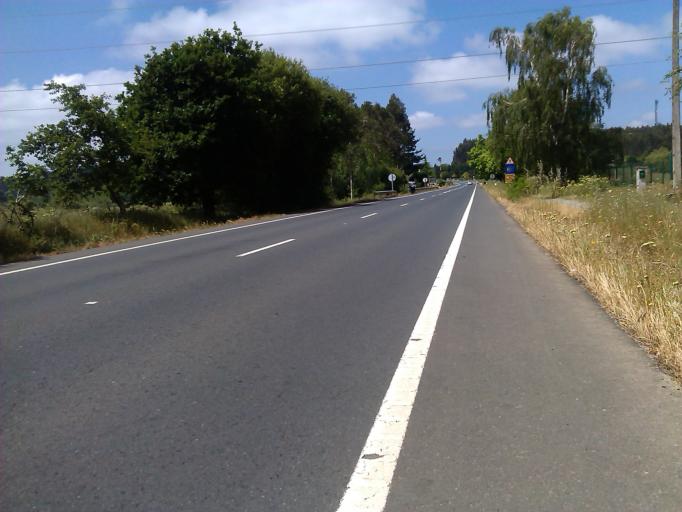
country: ES
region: Galicia
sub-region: Provincia da Coruna
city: Touro
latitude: 42.9172
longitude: -8.3128
